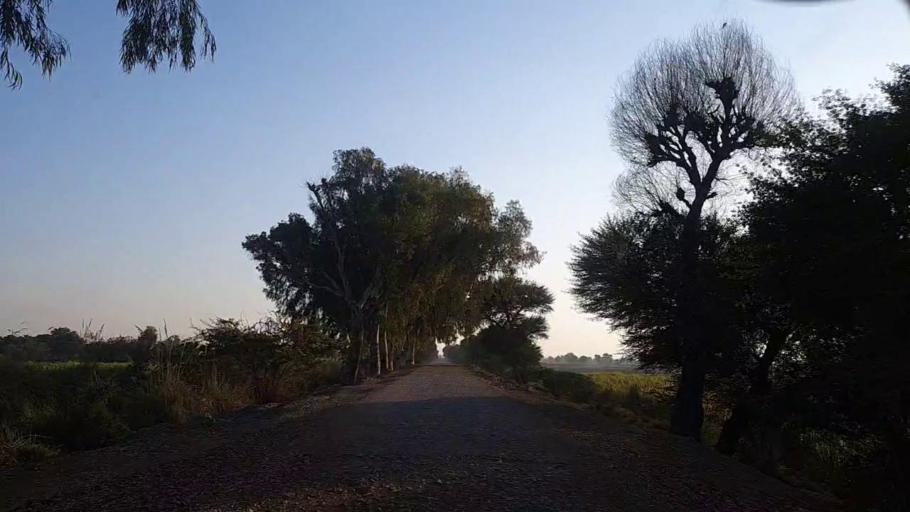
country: PK
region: Sindh
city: Sobhadero
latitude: 27.3816
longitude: 68.3811
